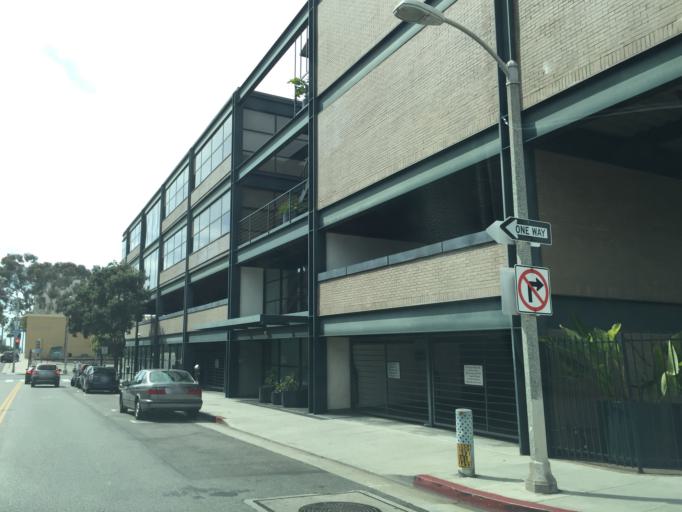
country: US
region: California
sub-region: Los Angeles County
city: Santa Monica
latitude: 33.9986
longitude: -118.4791
